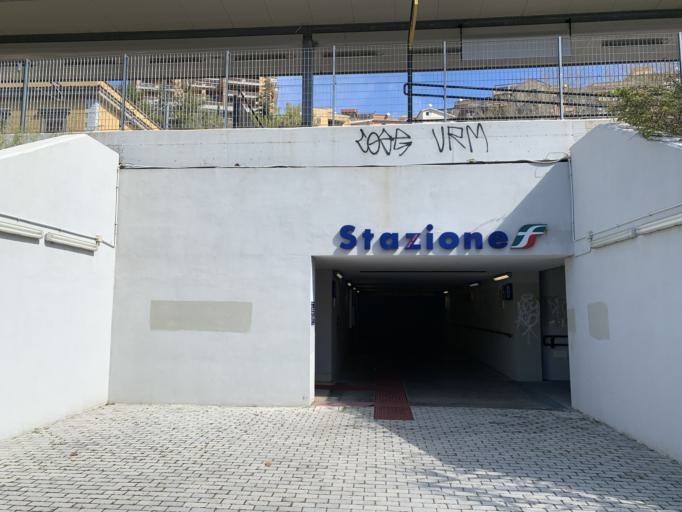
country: IT
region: Latium
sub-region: Citta metropolitana di Roma Capitale
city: Castel Gandolfo
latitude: 41.7688
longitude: 12.6562
